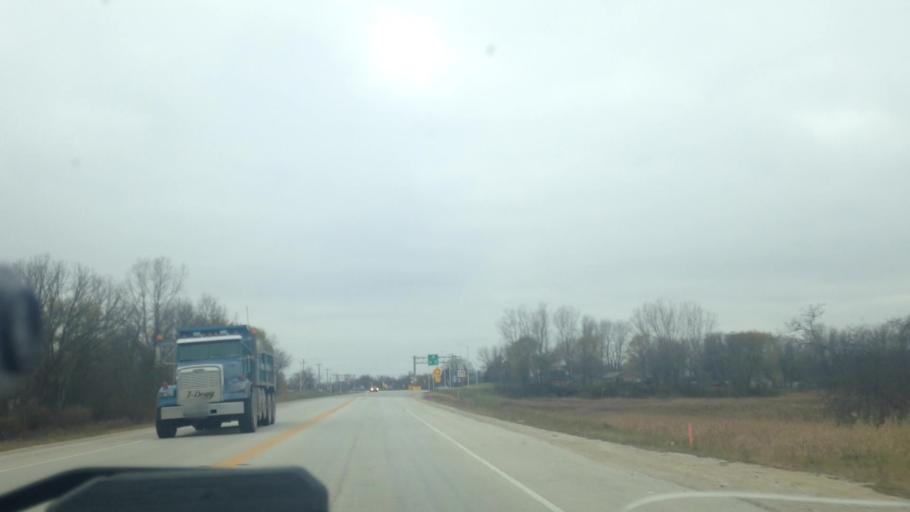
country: US
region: Wisconsin
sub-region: Waukesha County
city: Menomonee Falls
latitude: 43.2084
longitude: -88.1545
